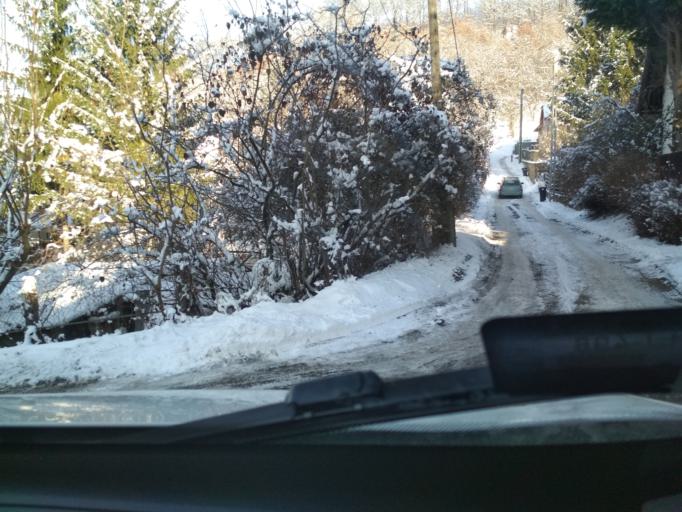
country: HU
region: Nograd
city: Salgotarjan
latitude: 48.1114
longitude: 19.8296
